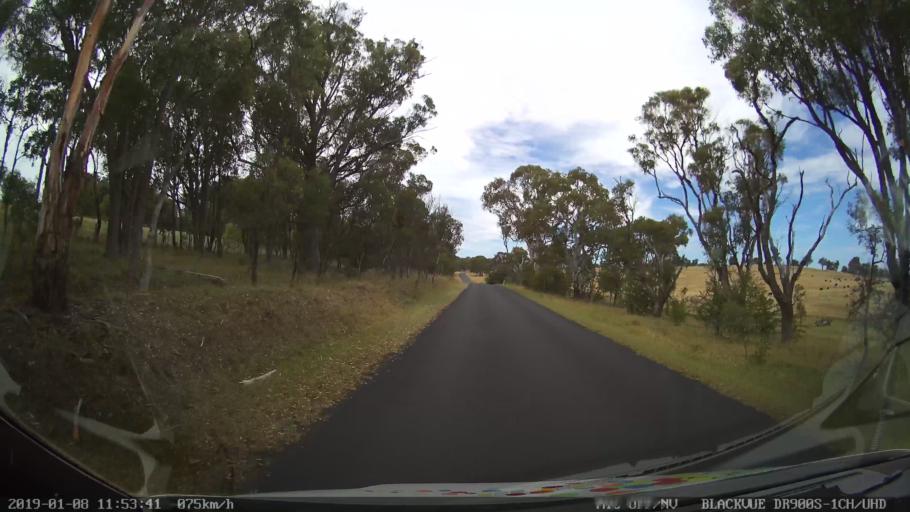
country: AU
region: New South Wales
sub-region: Armidale Dumaresq
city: Armidale
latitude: -30.4172
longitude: 151.5618
